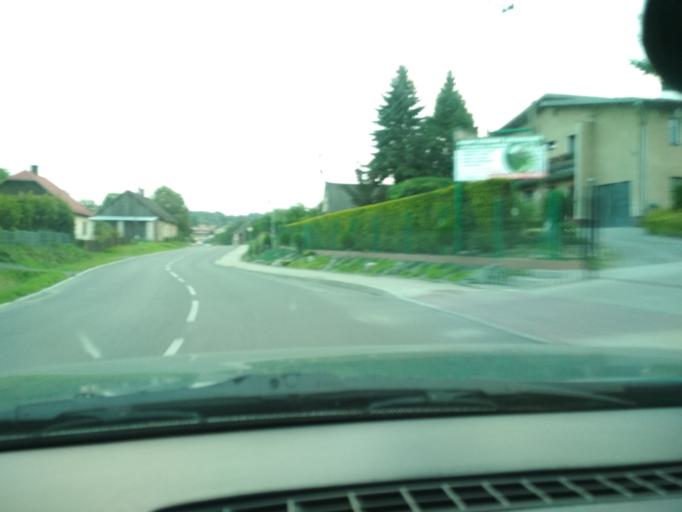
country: PL
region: Silesian Voivodeship
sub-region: Powiat bielski
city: Jasienica
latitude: 49.8413
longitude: 18.9405
